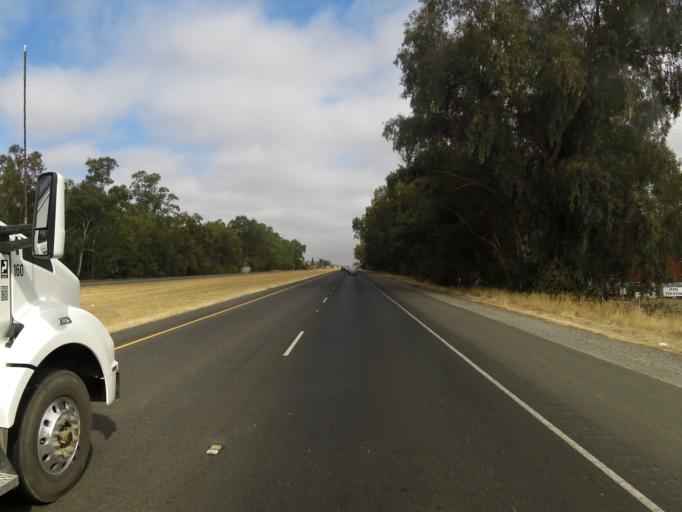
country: US
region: California
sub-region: Yolo County
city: Dunnigan
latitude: 38.8981
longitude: -121.9820
